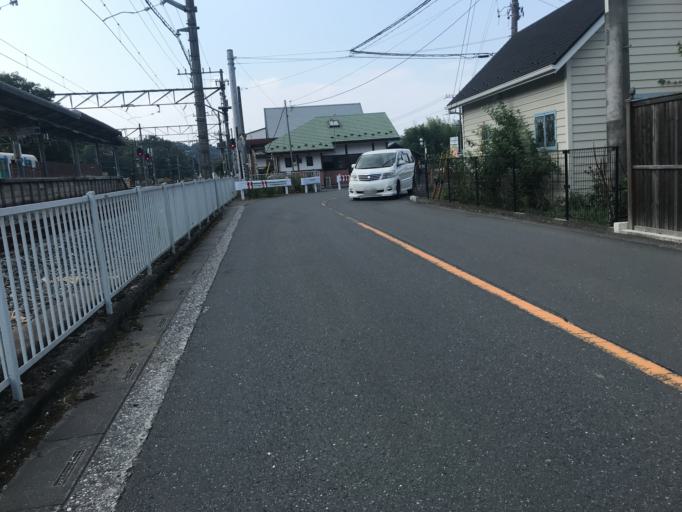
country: JP
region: Saitama
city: Chichibu
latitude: 35.9850
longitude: 139.0981
